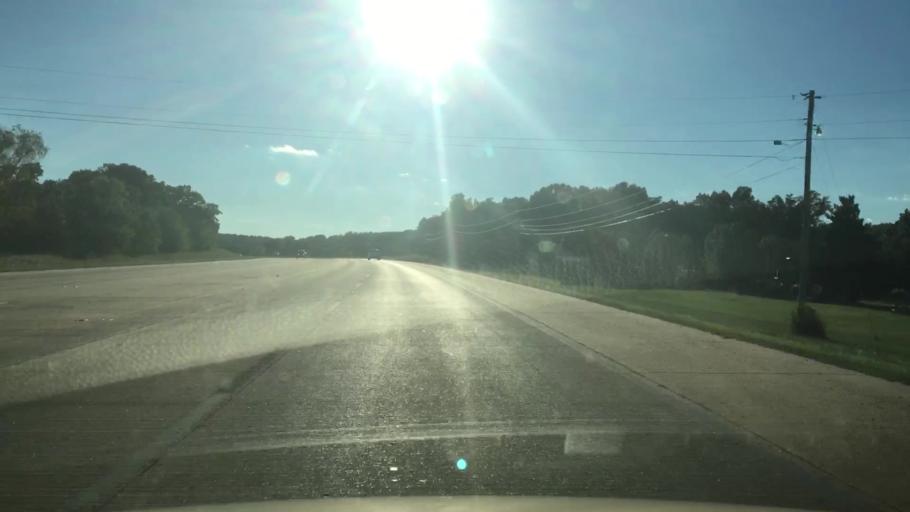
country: US
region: Oklahoma
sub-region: Cherokee County
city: Park Hill
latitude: 35.8482
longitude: -95.0226
